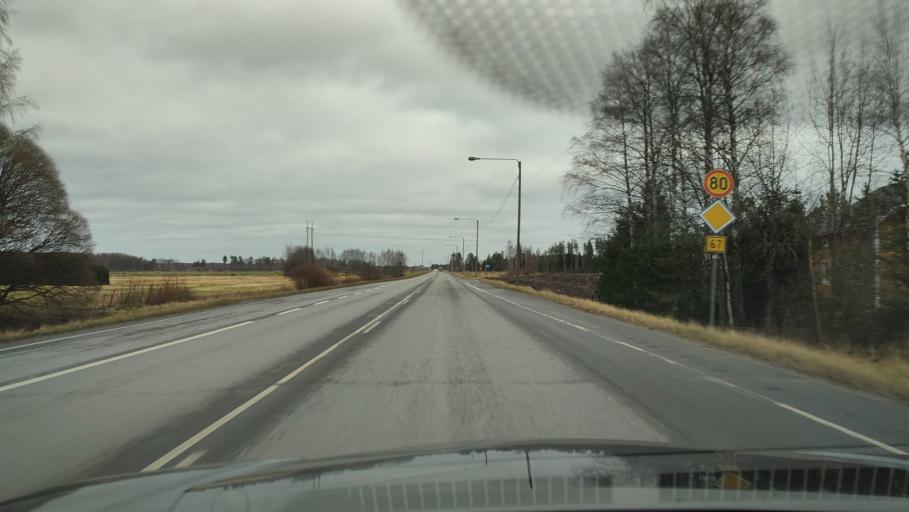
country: FI
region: Southern Ostrobothnia
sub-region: Seinaejoki
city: Kurikka
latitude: 62.6829
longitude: 22.4818
